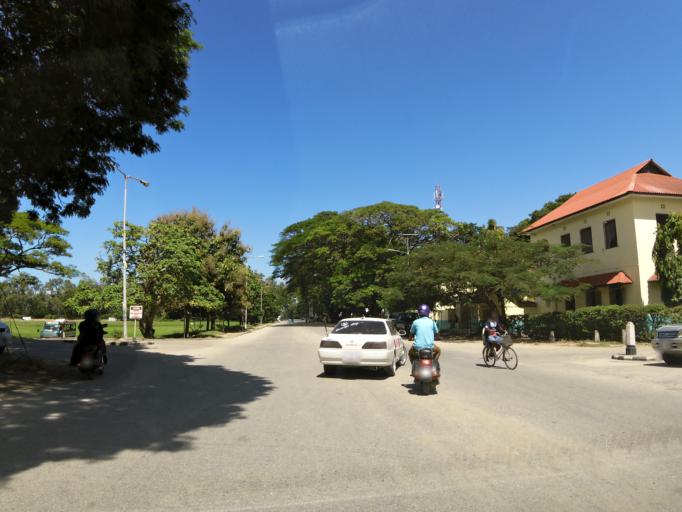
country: TZ
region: Zanzibar Urban/West
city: Zanzibar
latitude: -6.1661
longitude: 39.1924
